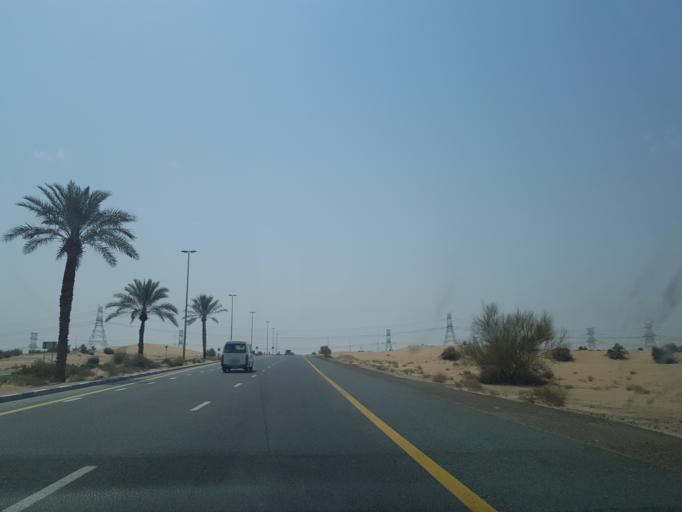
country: AE
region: Ash Shariqah
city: Sharjah
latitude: 25.1183
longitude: 55.4282
